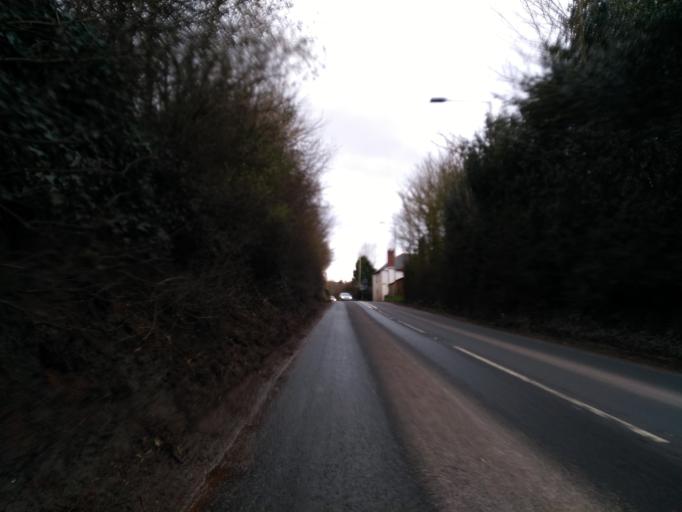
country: GB
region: England
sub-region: Devon
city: Crediton
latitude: 50.7755
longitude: -3.6063
